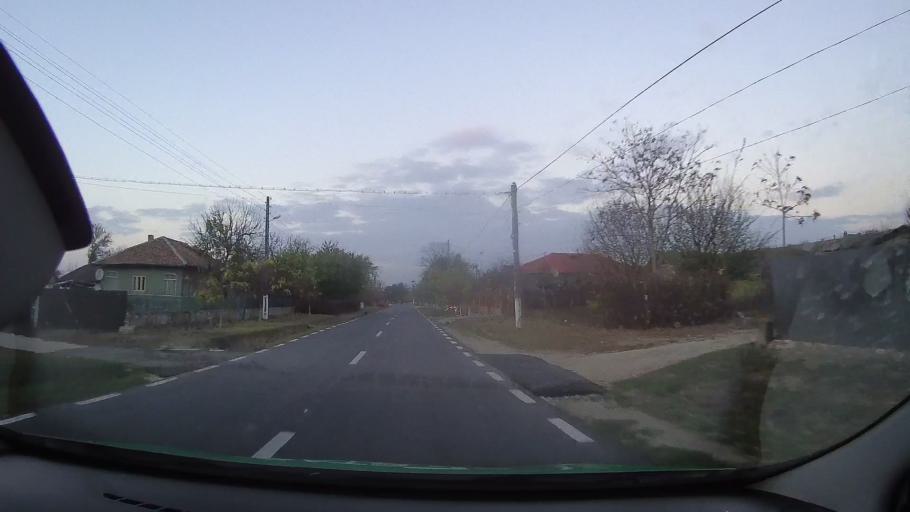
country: RO
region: Constanta
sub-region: Comuna Oltina
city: Oltina
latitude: 44.1603
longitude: 27.6676
